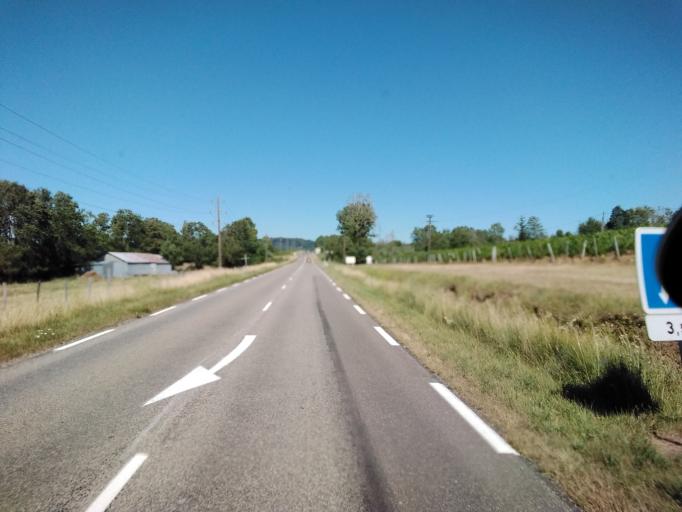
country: FR
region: Franche-Comte
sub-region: Departement du Jura
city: Arbois
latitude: 46.8987
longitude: 5.7437
